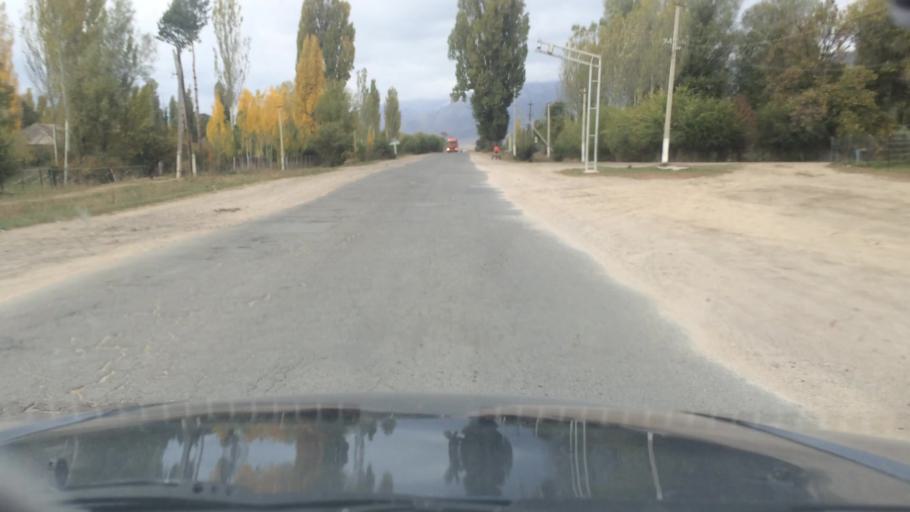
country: KG
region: Ysyk-Koel
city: Tyup
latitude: 42.7820
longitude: 78.2887
